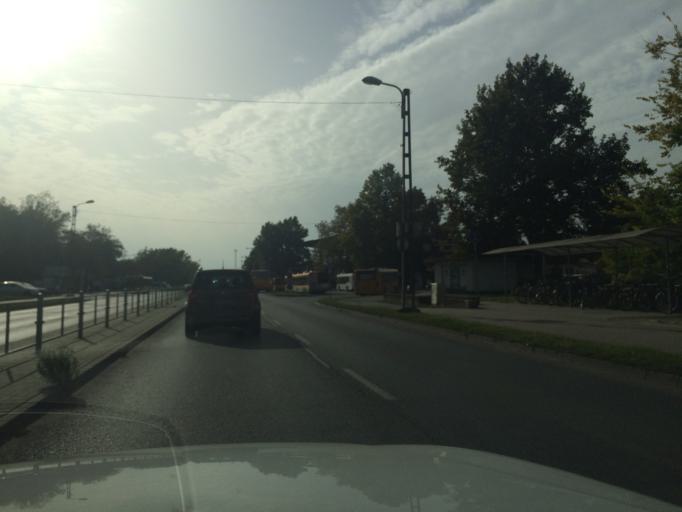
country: HU
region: Szabolcs-Szatmar-Bereg
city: Nyiregyhaza
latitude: 47.9483
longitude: 21.7061
